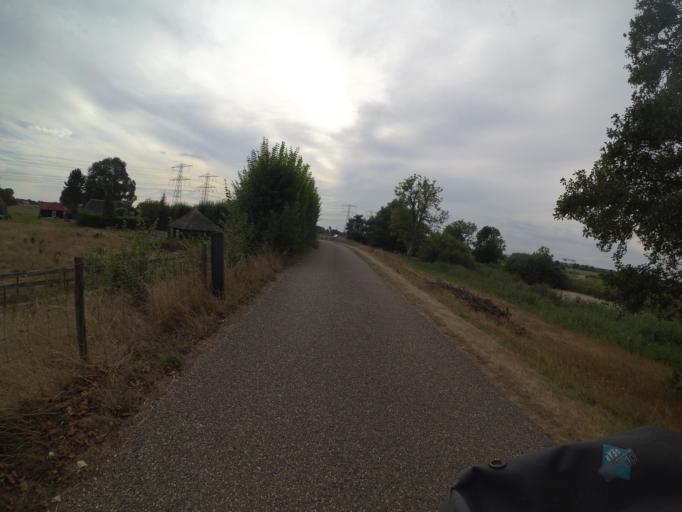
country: NL
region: Overijssel
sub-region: Gemeente Zwartewaterland
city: Hasselt
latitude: 52.5752
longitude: 6.1129
